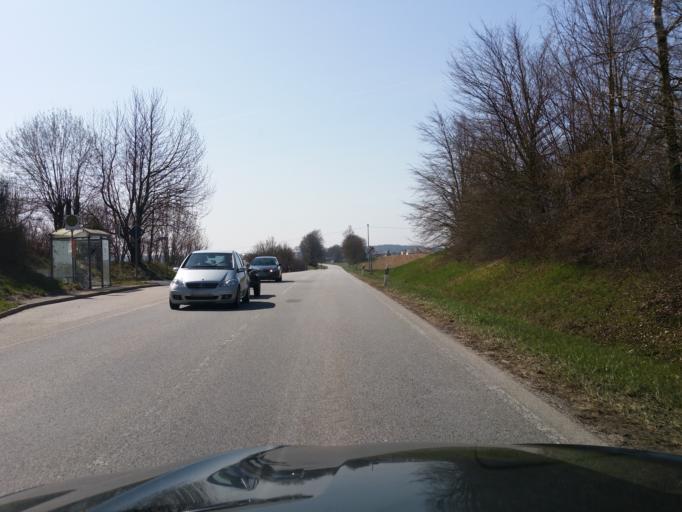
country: DE
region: Bavaria
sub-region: Lower Bavaria
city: Altfraunhofen
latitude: 48.4645
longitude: 12.1514
